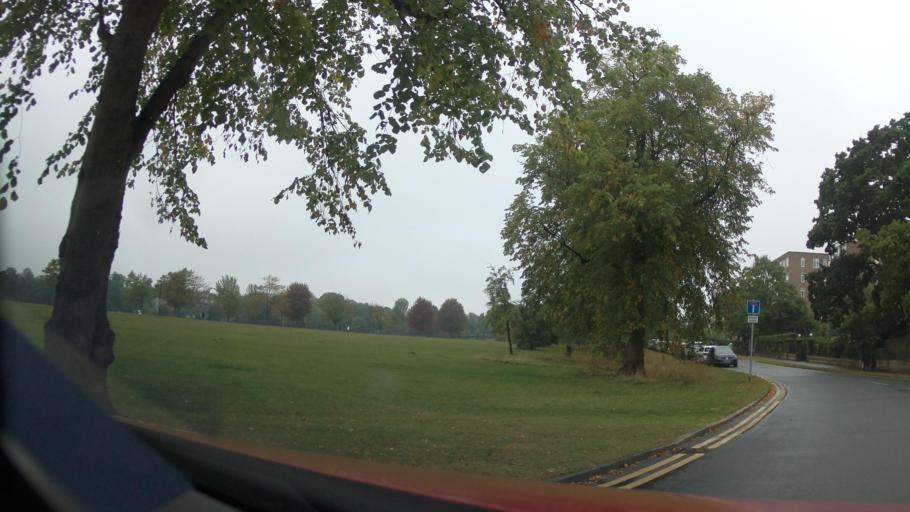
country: GB
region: England
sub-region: North Yorkshire
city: Harrogate
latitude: 53.9900
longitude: -1.5426
